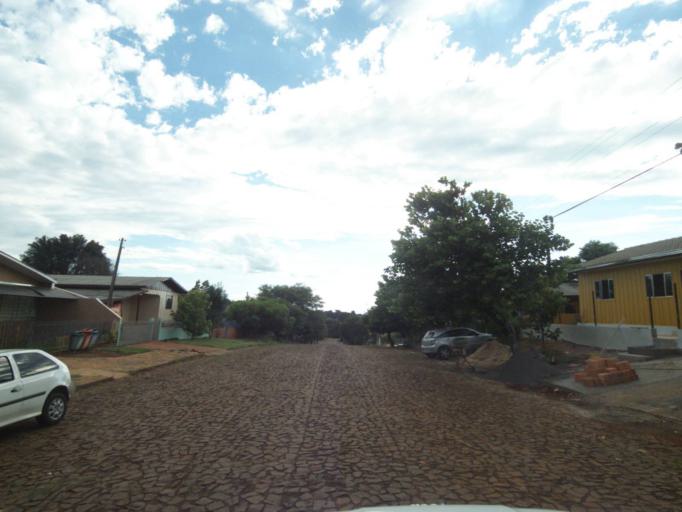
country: BR
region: Parana
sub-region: Laranjeiras Do Sul
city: Laranjeiras do Sul
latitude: -25.4921
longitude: -52.5257
